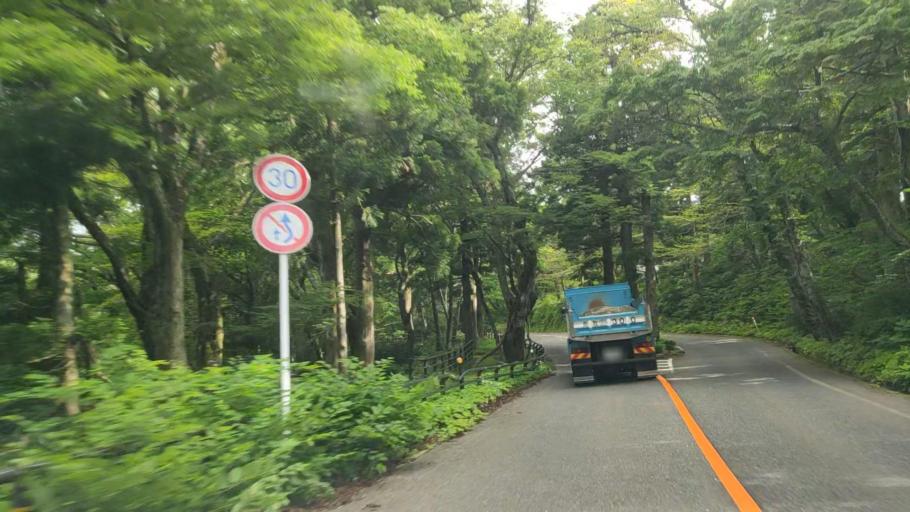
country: JP
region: Tottori
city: Yonago
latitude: 35.3885
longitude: 133.5284
